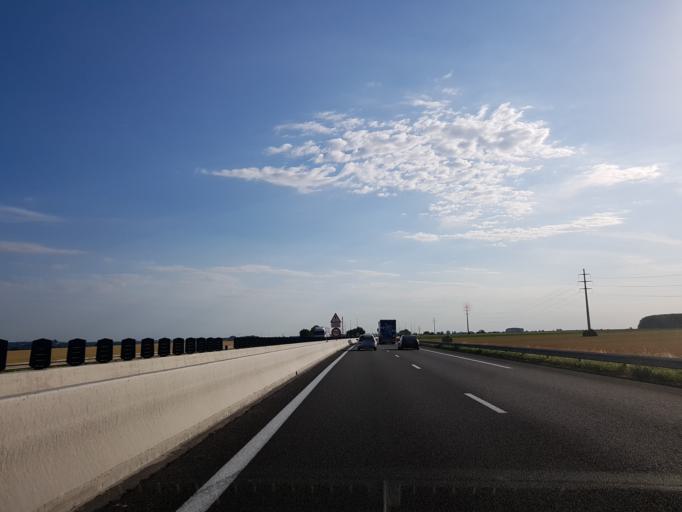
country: FR
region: Nord-Pas-de-Calais
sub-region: Departement du Nord
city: Escaudoeuvres
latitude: 50.2325
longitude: 3.2797
